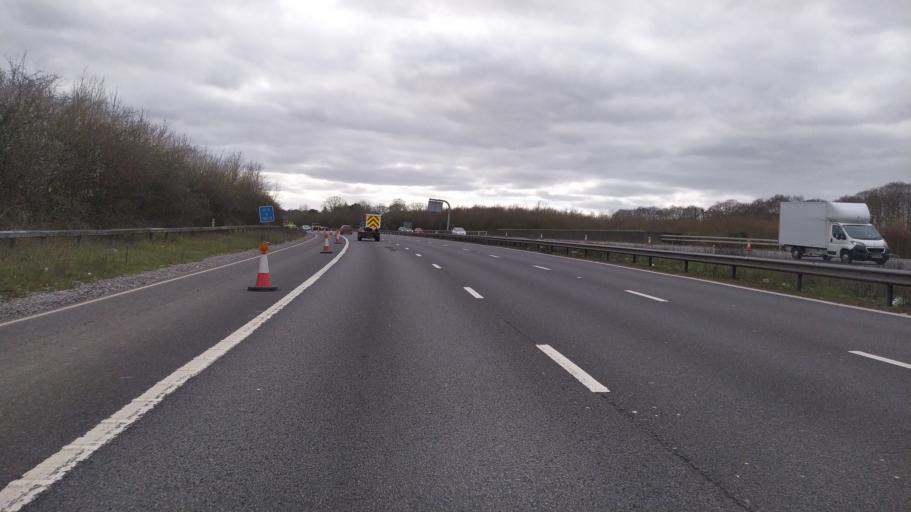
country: GB
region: England
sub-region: Hampshire
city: Compton
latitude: 51.0336
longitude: -1.3248
